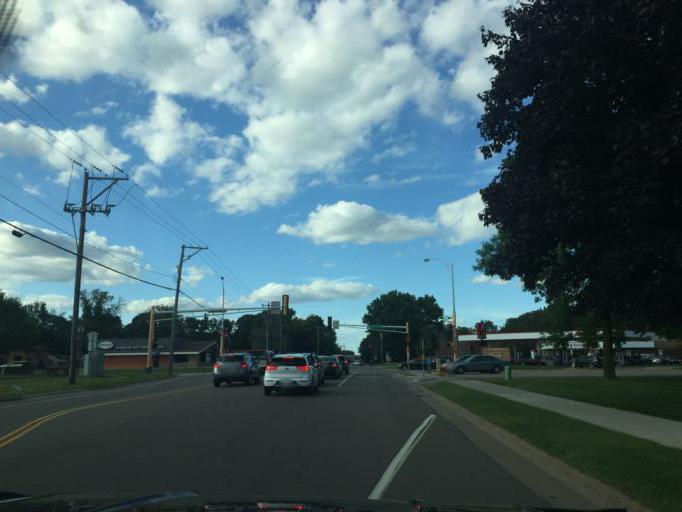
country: US
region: Minnesota
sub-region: Ramsey County
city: Roseville
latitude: 45.0058
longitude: -93.1463
